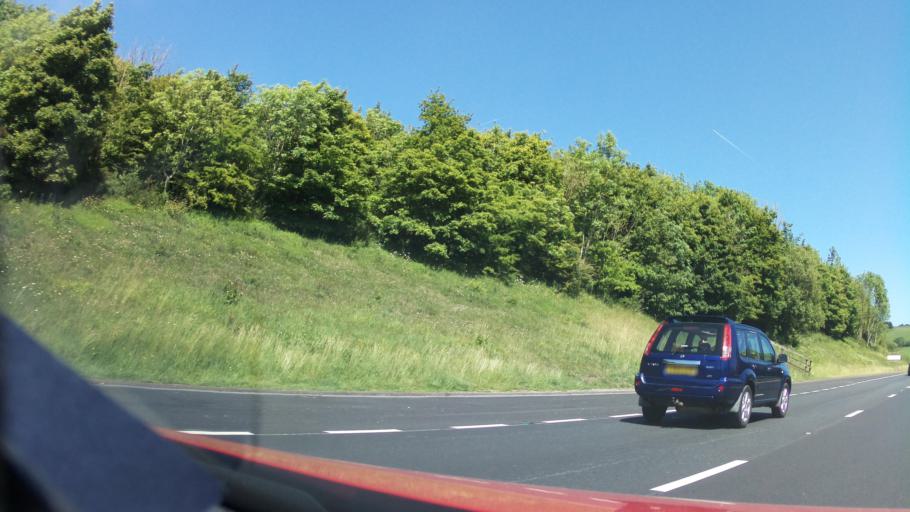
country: GB
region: England
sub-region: Devon
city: Bovey Tracey
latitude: 50.5423
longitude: -3.7016
